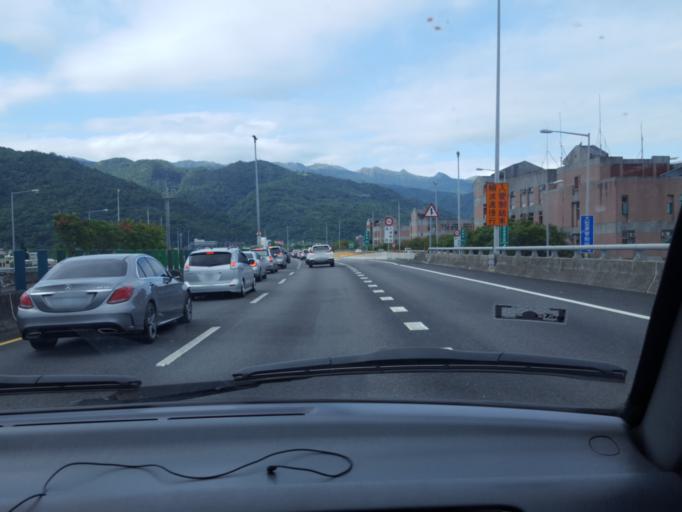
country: TW
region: Taiwan
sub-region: Yilan
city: Yilan
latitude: 24.8317
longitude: 121.7909
